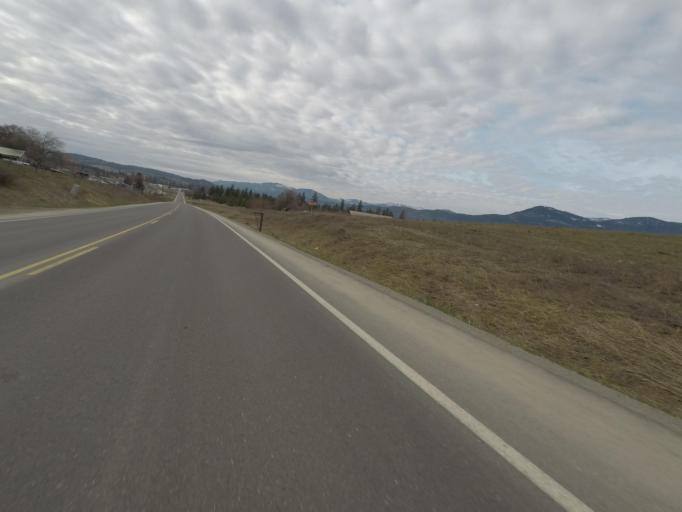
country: US
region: Washington
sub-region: Stevens County
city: Colville
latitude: 48.5548
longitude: -117.8821
